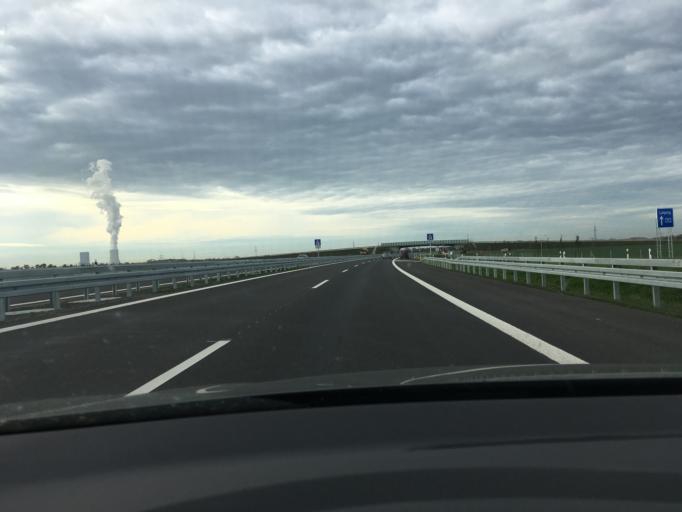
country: DE
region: Saxony
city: Espenhain
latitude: 51.1833
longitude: 12.4617
